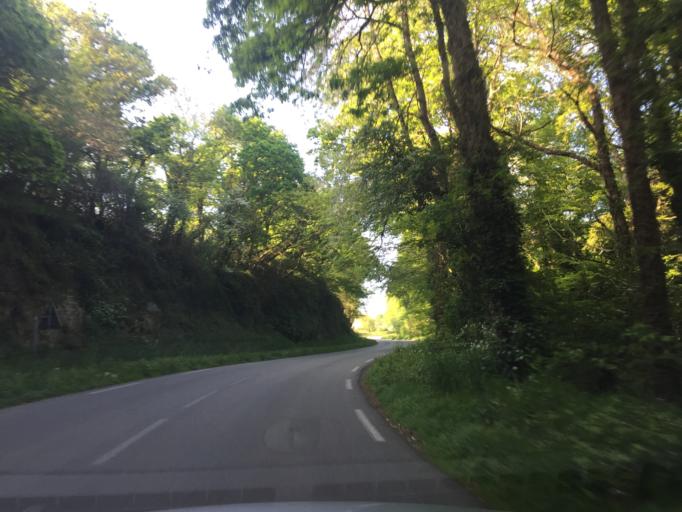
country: FR
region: Brittany
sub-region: Departement des Cotes-d'Armor
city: Crehen
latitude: 48.5748
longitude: -2.2368
